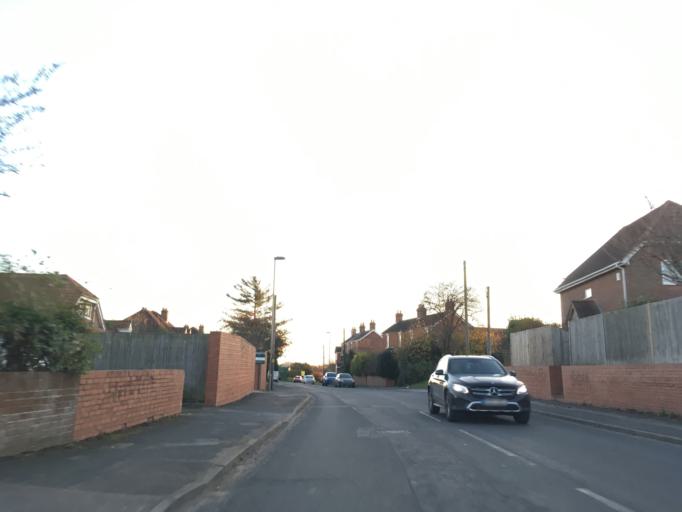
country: GB
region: England
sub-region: Hampshire
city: Bishopstoke
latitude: 50.9699
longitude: -1.3035
